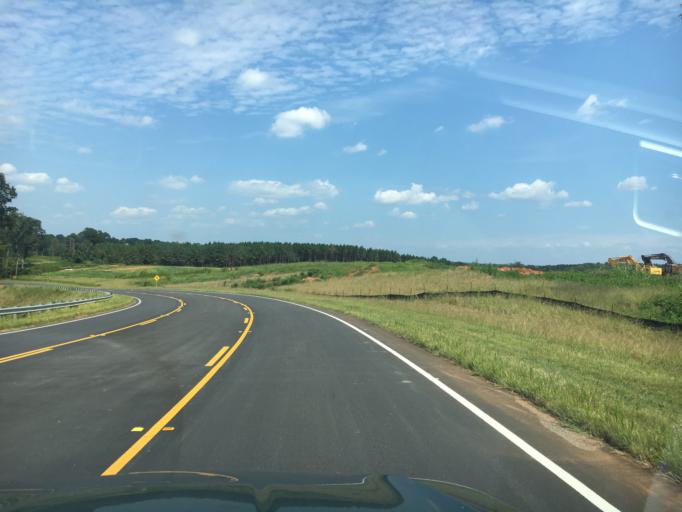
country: US
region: South Carolina
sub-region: Spartanburg County
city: Roebuck
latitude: 34.8723
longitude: -82.0281
